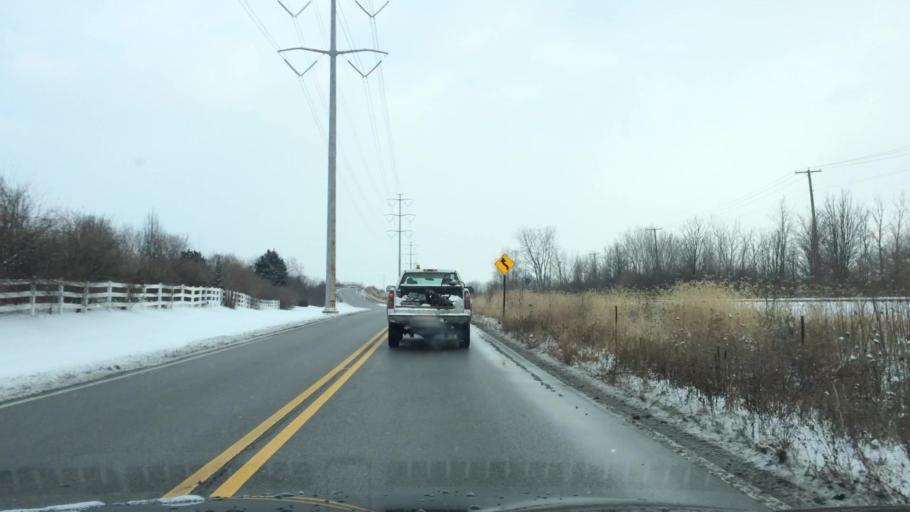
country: US
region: Ohio
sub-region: Franklin County
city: Hilliard
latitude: 40.0169
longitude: -83.1327
